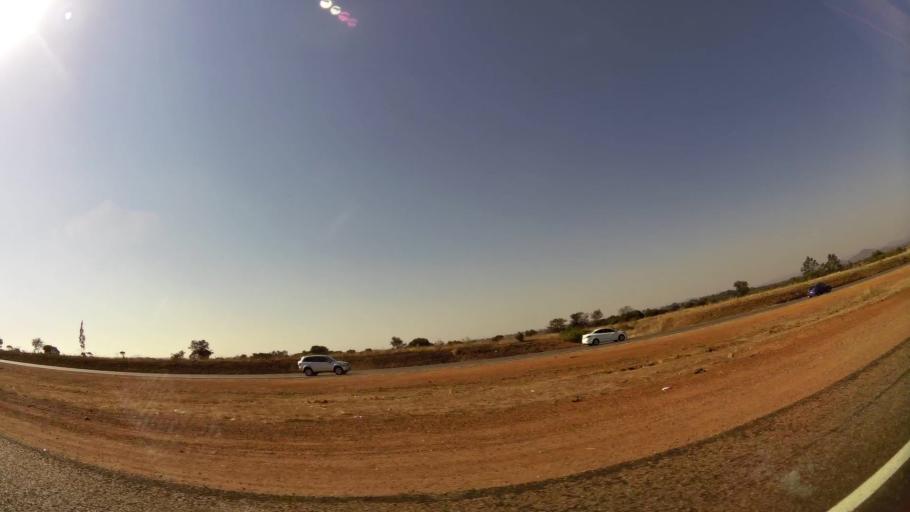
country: ZA
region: Gauteng
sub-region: City of Tshwane Metropolitan Municipality
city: Mabopane
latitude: -25.5684
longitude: 28.1076
